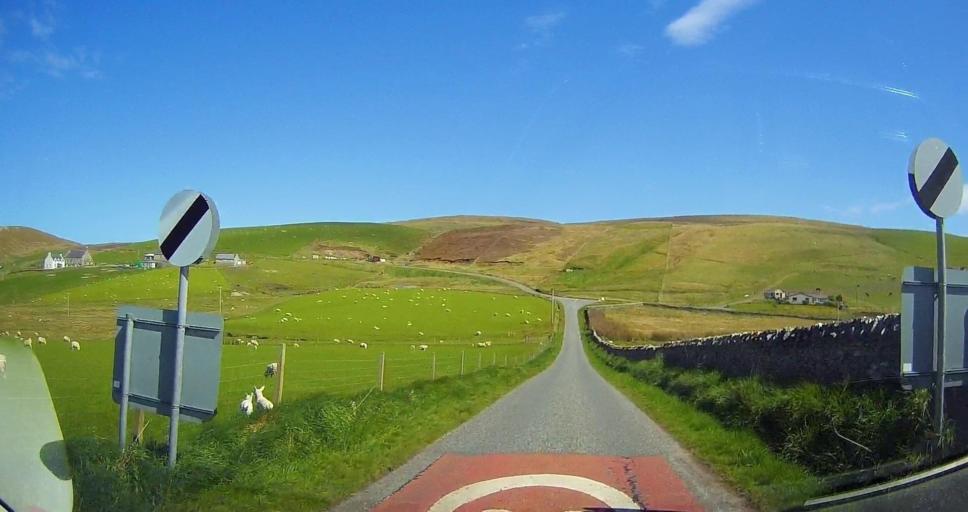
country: GB
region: Scotland
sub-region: Shetland Islands
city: Sandwick
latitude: 59.9726
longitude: -1.3195
